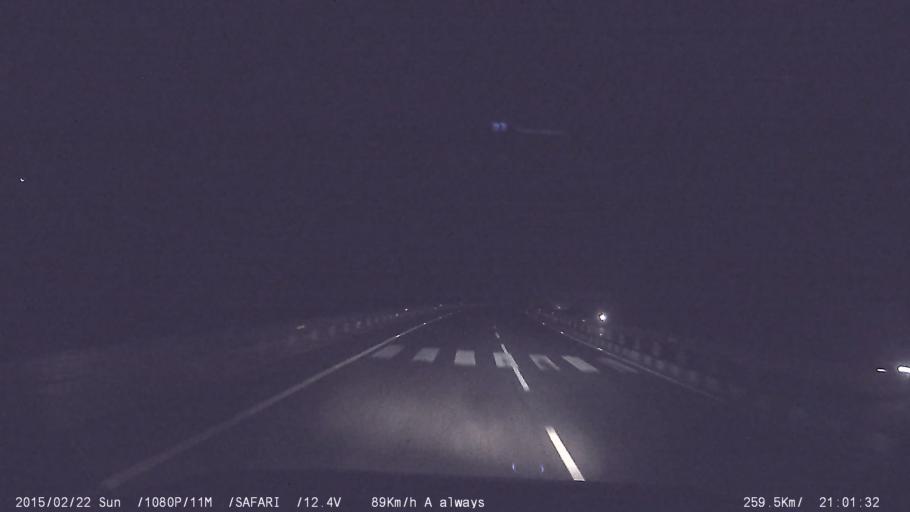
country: IN
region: Tamil Nadu
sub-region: Karur
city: Pallappatti
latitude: 10.6657
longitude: 77.9334
